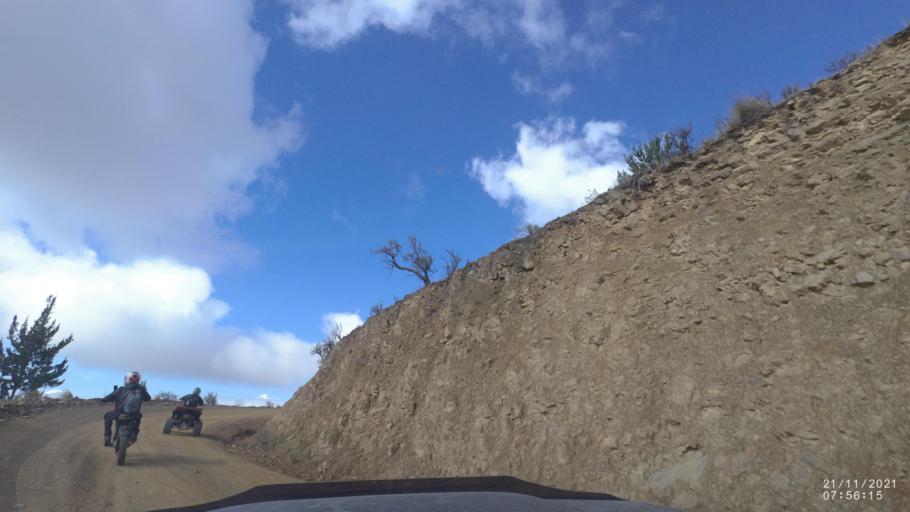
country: BO
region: Cochabamba
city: Cochabamba
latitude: -17.2976
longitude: -66.2174
